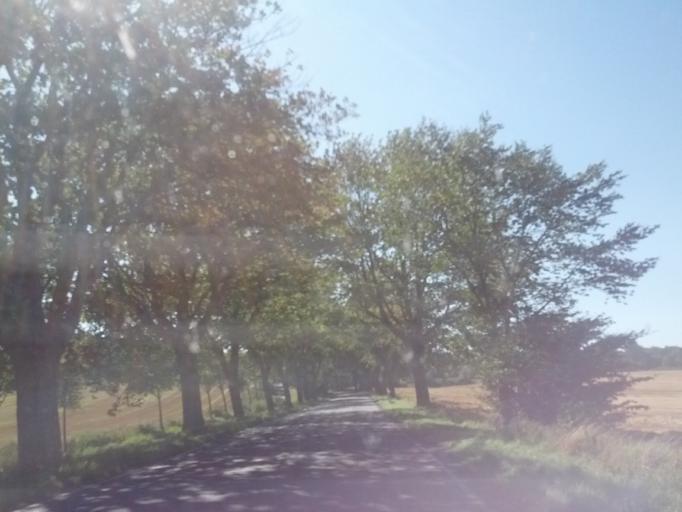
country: DE
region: Mecklenburg-Vorpommern
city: Bergen auf Ruegen
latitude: 54.4284
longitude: 13.4325
